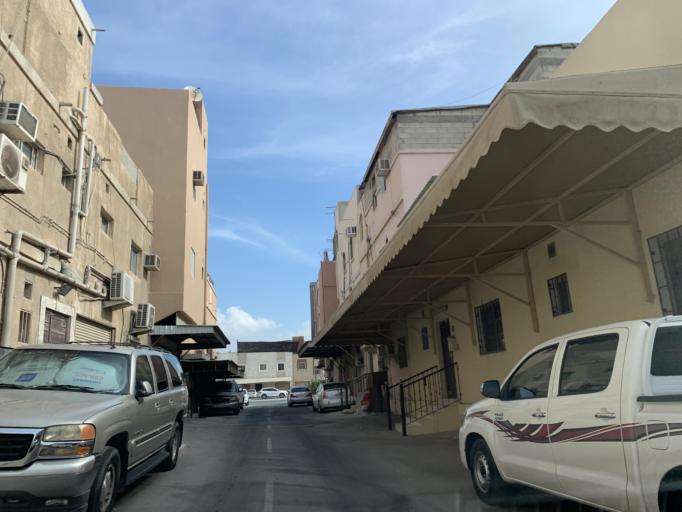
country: BH
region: Central Governorate
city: Madinat Hamad
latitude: 26.1268
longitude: 50.4767
